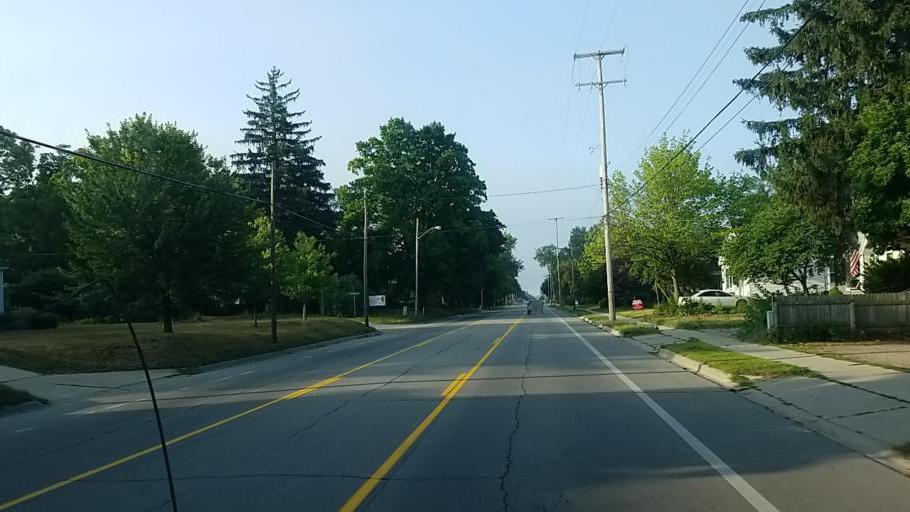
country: US
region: Michigan
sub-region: Newaygo County
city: Fremont
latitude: 43.4629
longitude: -85.9401
